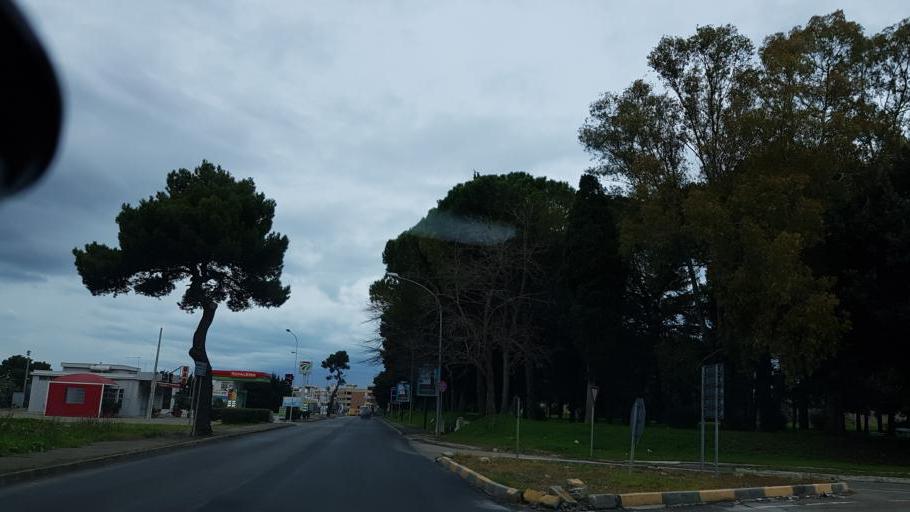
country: IT
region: Apulia
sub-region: Provincia di Brindisi
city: Brindisi
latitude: 40.6262
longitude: 17.9478
